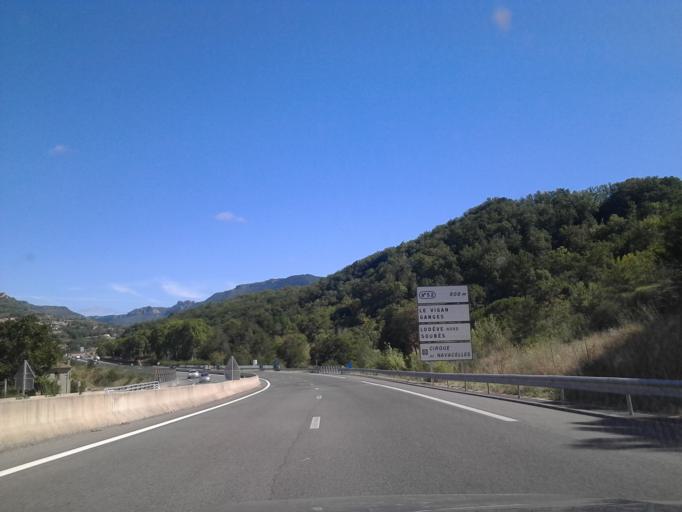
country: FR
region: Languedoc-Roussillon
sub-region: Departement de l'Herault
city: Lodeve
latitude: 43.7456
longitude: 3.3309
